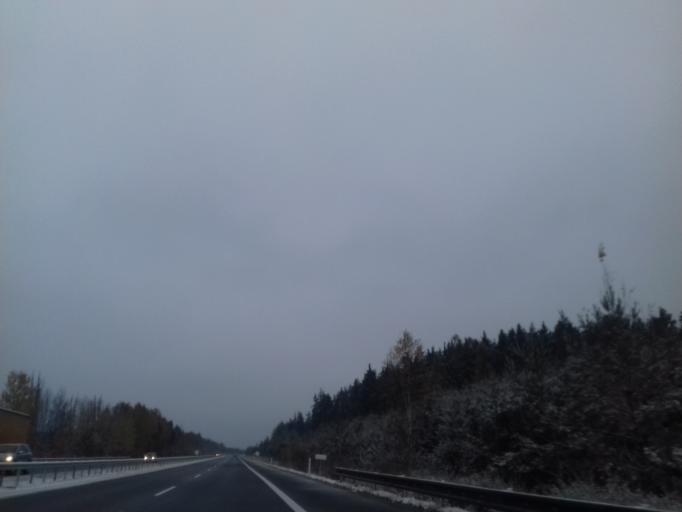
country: CZ
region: Plzensky
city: Myto
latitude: 49.8121
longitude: 13.7592
